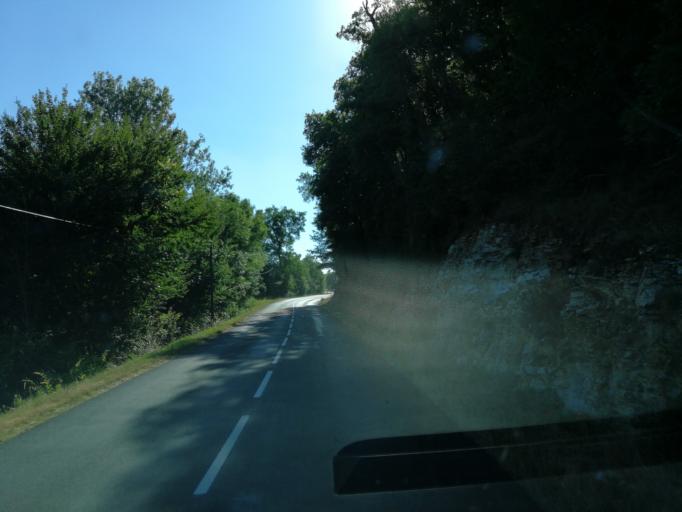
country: FR
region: Midi-Pyrenees
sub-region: Departement du Lot
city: Salviac
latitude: 44.7114
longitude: 1.3201
